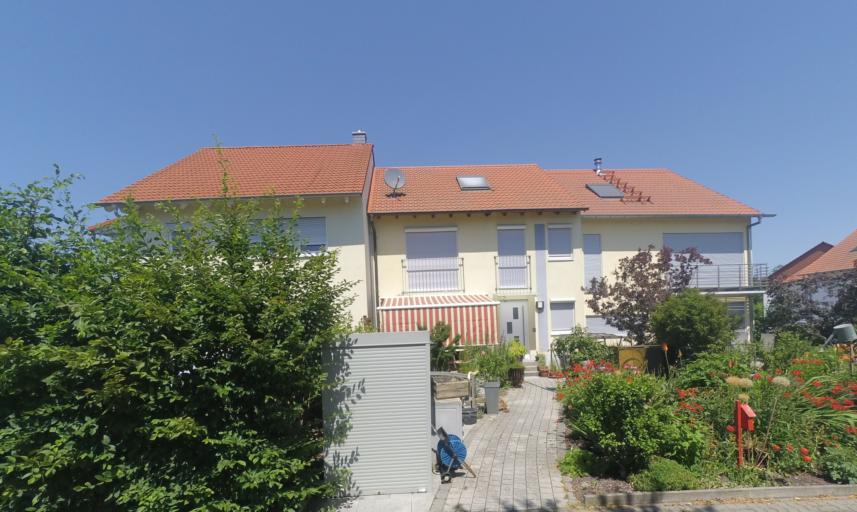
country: DE
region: Rheinland-Pfalz
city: Limburgerhof
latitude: 49.4258
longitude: 8.4014
